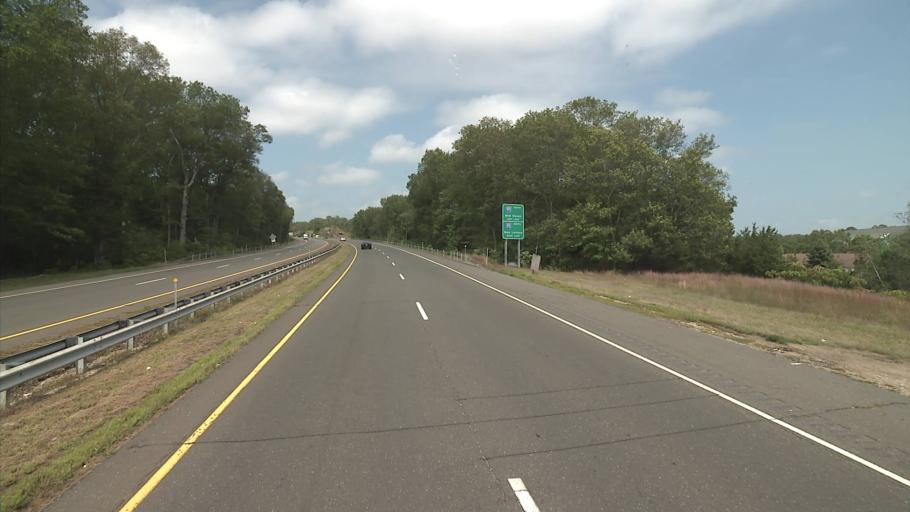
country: US
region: Connecticut
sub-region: New London County
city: Niantic
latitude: 41.3180
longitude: -72.2456
